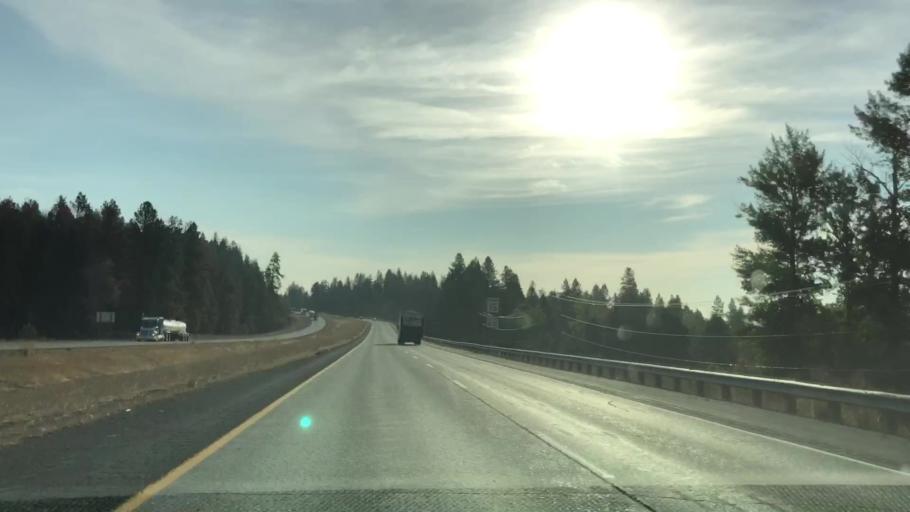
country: US
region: Washington
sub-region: Kittitas County
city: Cle Elum
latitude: 47.1835
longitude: -121.0029
